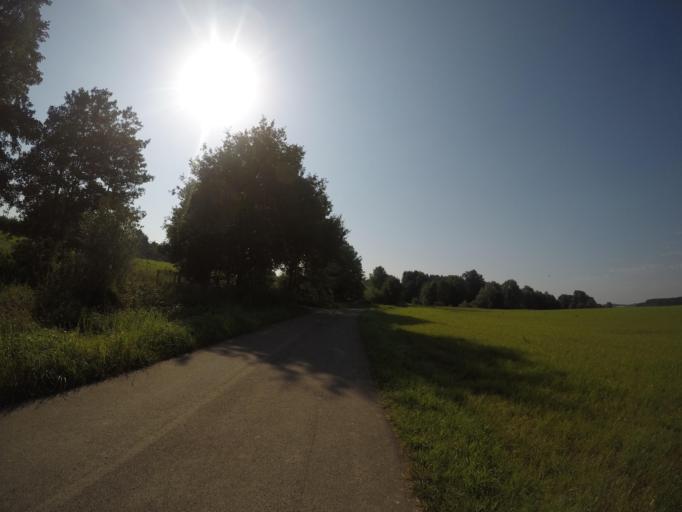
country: DE
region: Baden-Wuerttemberg
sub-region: Tuebingen Region
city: Wain
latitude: 48.2067
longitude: 10.0187
